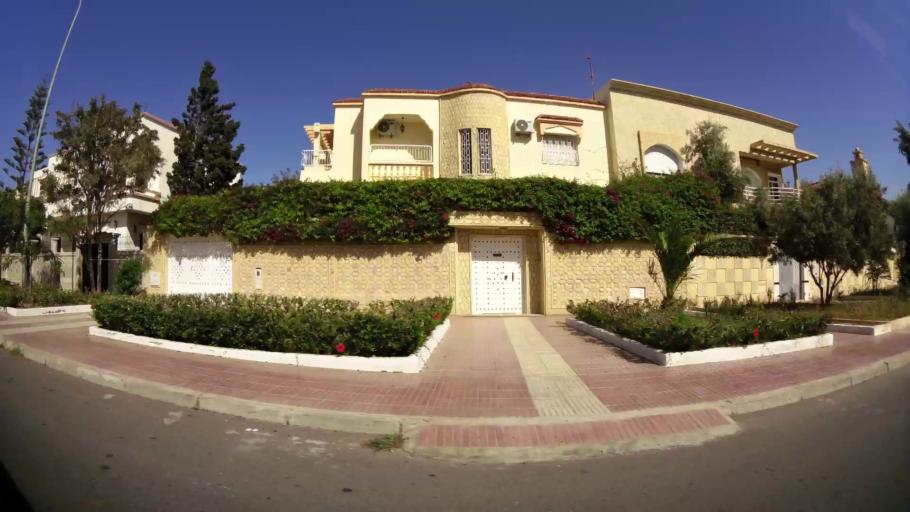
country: MA
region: Souss-Massa-Draa
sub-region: Inezgane-Ait Mellou
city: Inezgane
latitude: 30.3615
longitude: -9.5500
